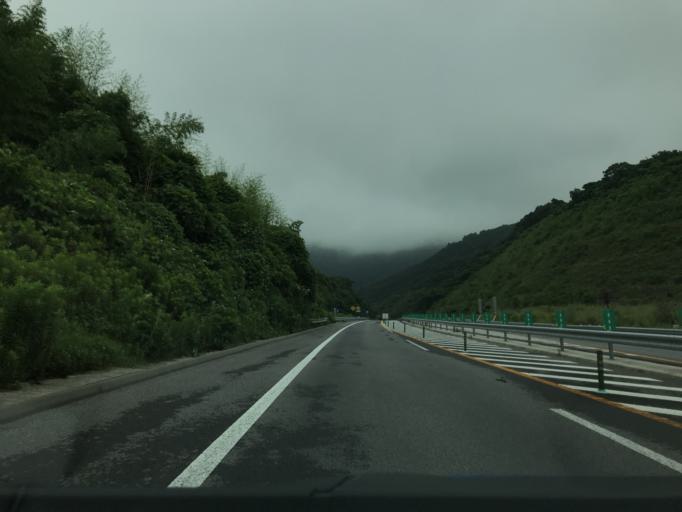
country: JP
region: Oita
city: Bungo-Takada-shi
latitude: 33.4977
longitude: 131.3176
